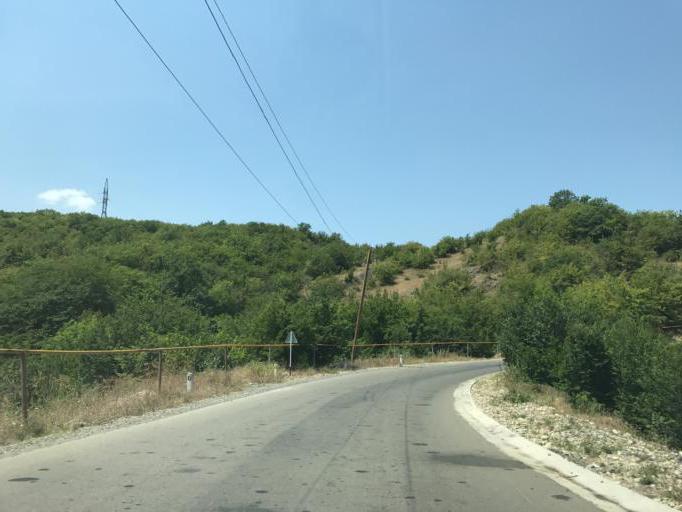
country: AZ
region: Tartar Rayon
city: Martakert
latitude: 40.1413
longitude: 46.5937
